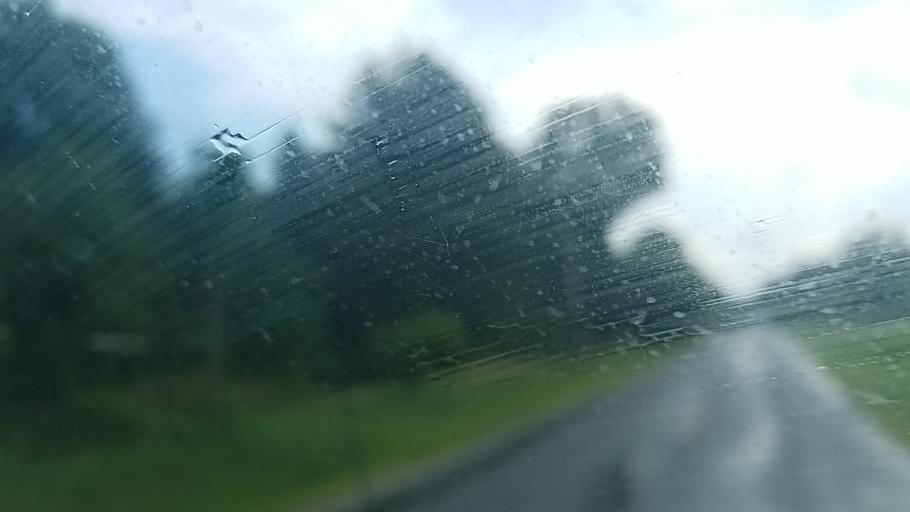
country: US
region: Ohio
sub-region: Lorain County
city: Grafton
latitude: 41.1848
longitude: -82.0158
